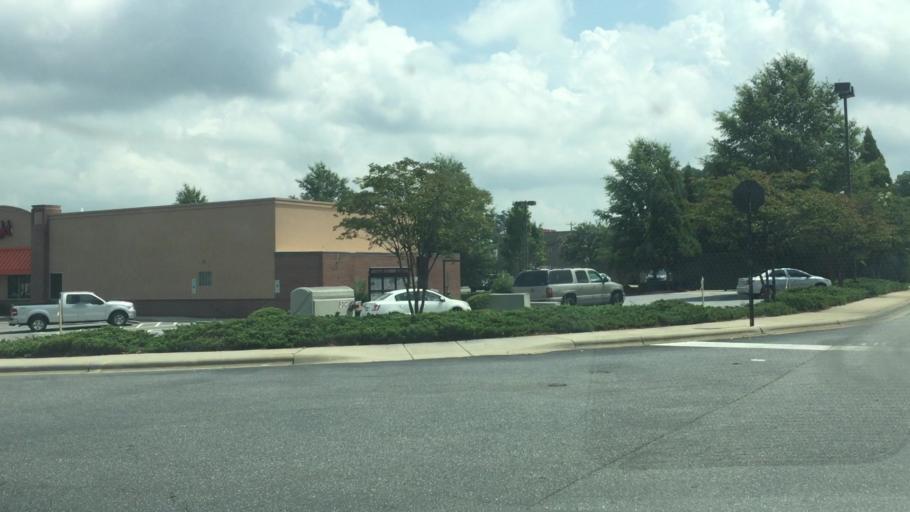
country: US
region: North Carolina
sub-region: Iredell County
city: Mooresville
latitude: 35.5949
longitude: -80.8748
